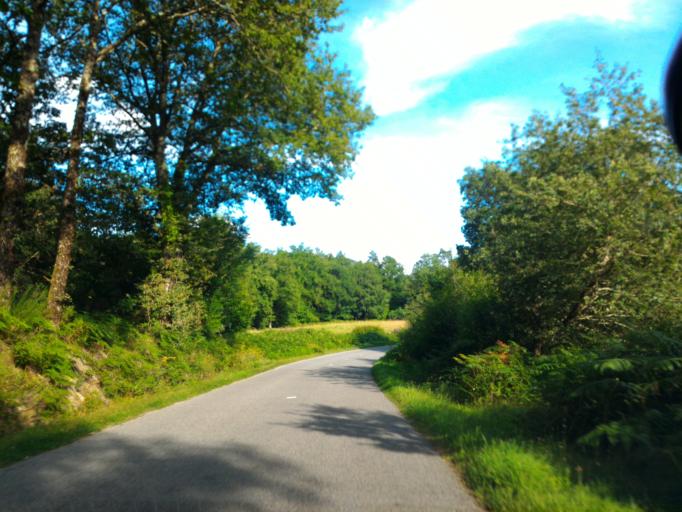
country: FR
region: Poitou-Charentes
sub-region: Departement de la Charente
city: Brigueuil
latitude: 45.9926
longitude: 0.8796
